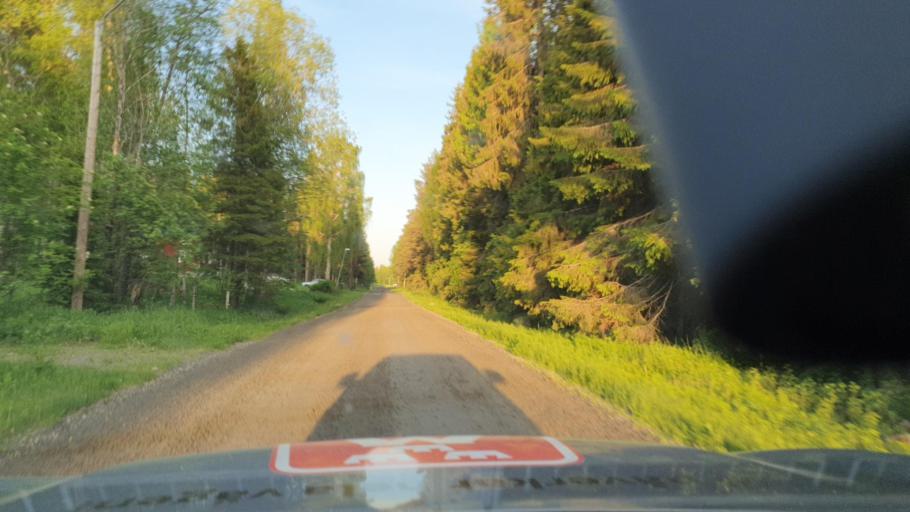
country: SE
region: Norrbotten
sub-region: Bodens Kommun
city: Boden
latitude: 66.1071
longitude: 21.5712
